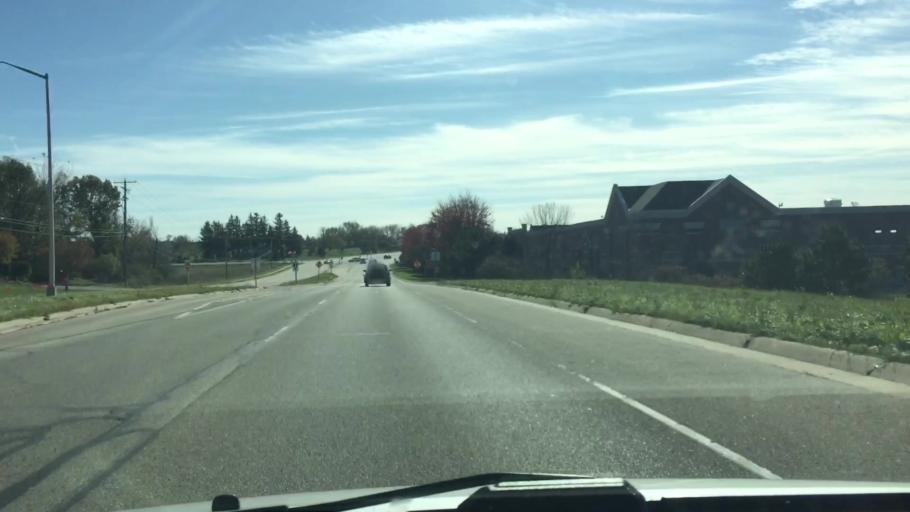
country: US
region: Wisconsin
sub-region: Waukesha County
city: Pewaukee
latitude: 43.0893
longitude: -88.2283
